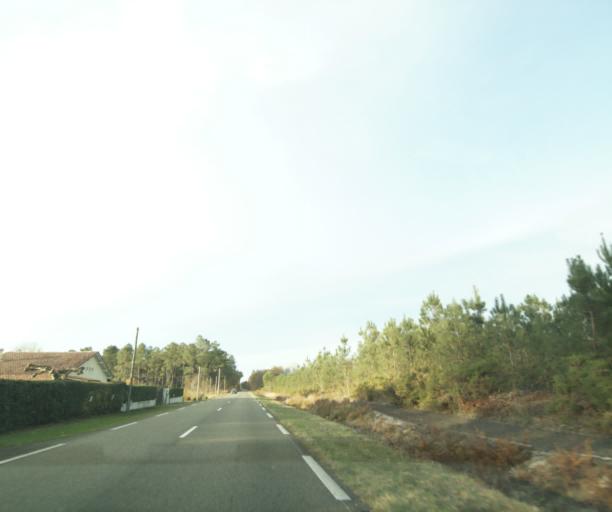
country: FR
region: Aquitaine
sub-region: Departement des Landes
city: Gabarret
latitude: 44.0298
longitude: -0.0288
